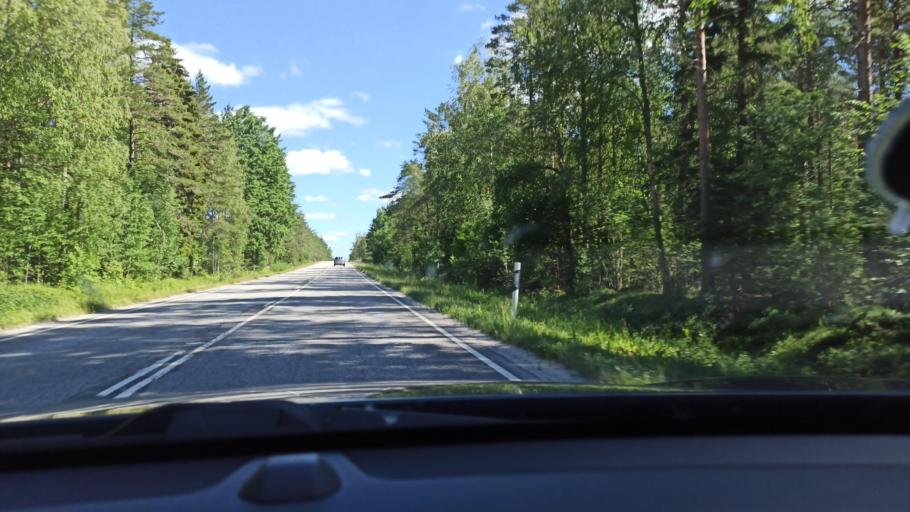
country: FI
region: Ostrobothnia
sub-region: Vaasa
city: Malax
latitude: 62.9804
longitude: 21.6177
